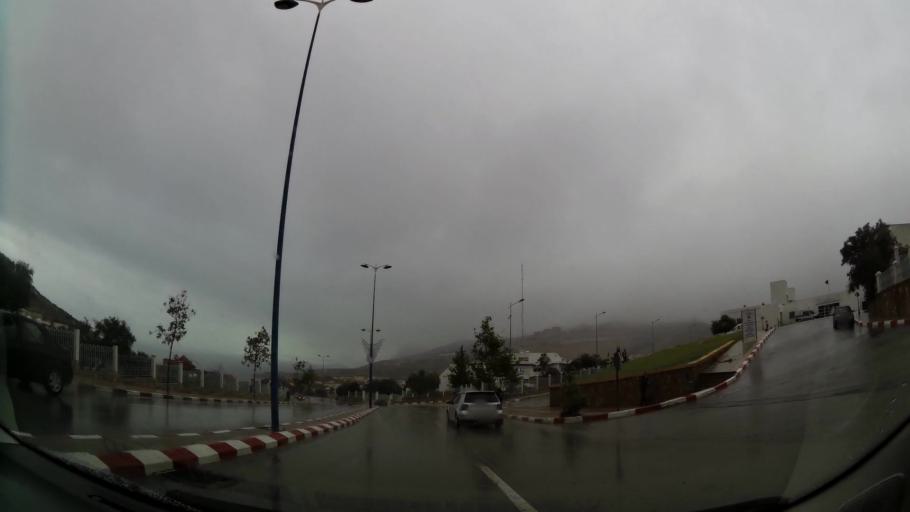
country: MA
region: Taza-Al Hoceima-Taounate
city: Al Hoceima
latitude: 35.2382
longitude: -3.9278
